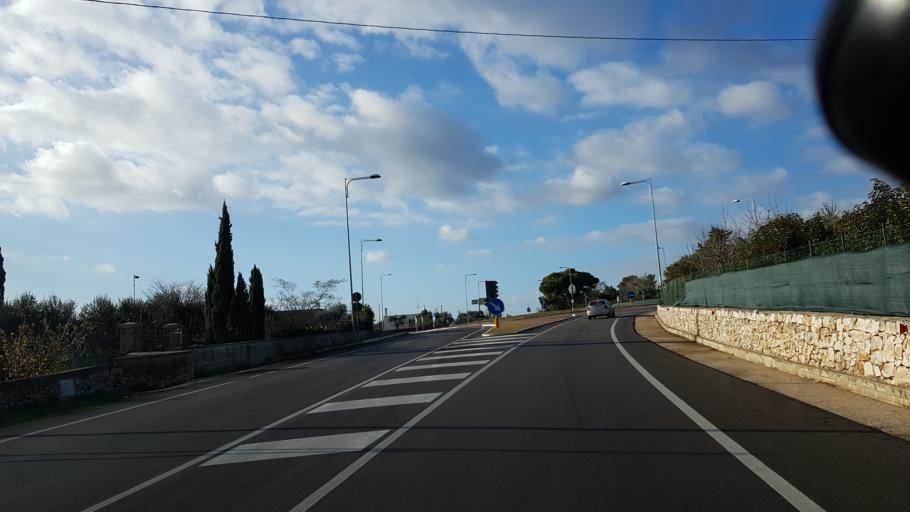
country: IT
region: Apulia
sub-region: Provincia di Bari
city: Putignano
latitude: 40.8401
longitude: 17.1493
